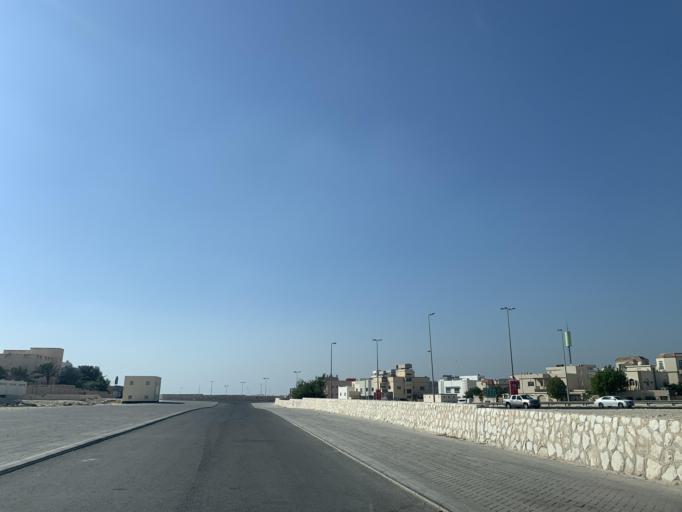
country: BH
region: Central Governorate
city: Madinat Hamad
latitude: 26.1204
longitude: 50.5069
